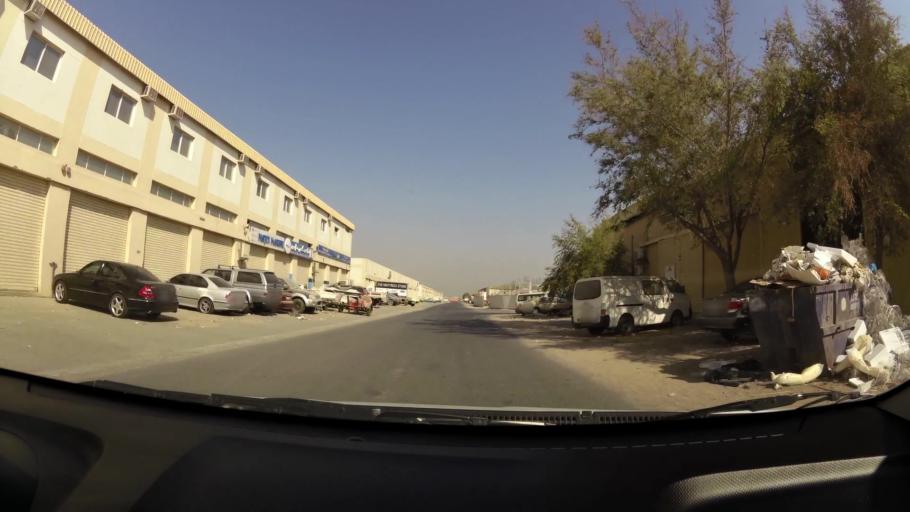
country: AE
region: Ajman
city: Ajman
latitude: 25.4345
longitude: 55.5139
